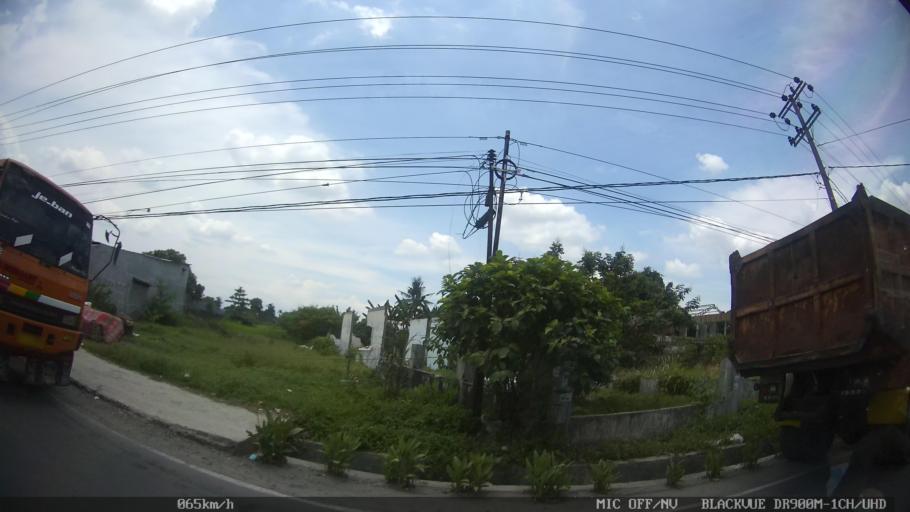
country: ID
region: North Sumatra
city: Binjai
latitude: 3.6013
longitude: 98.5436
